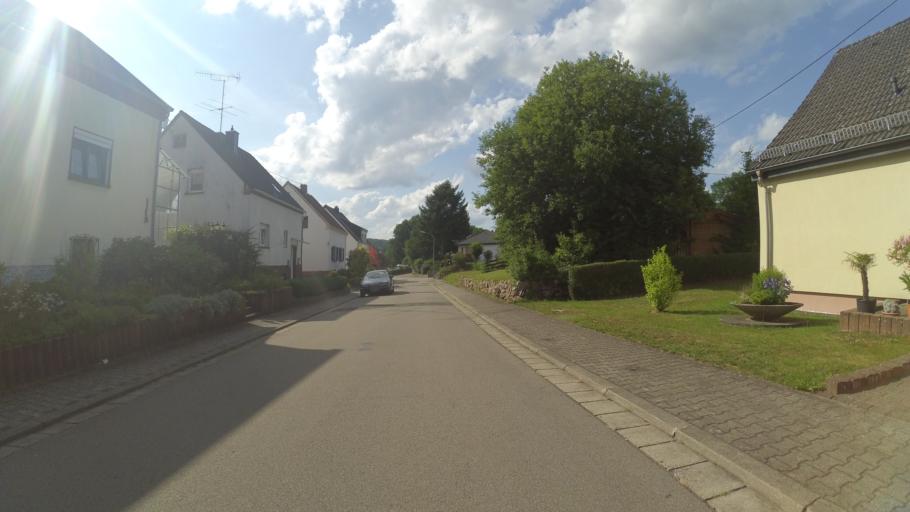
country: DE
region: Saarland
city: Nohfelden
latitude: 49.5799
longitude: 7.1483
